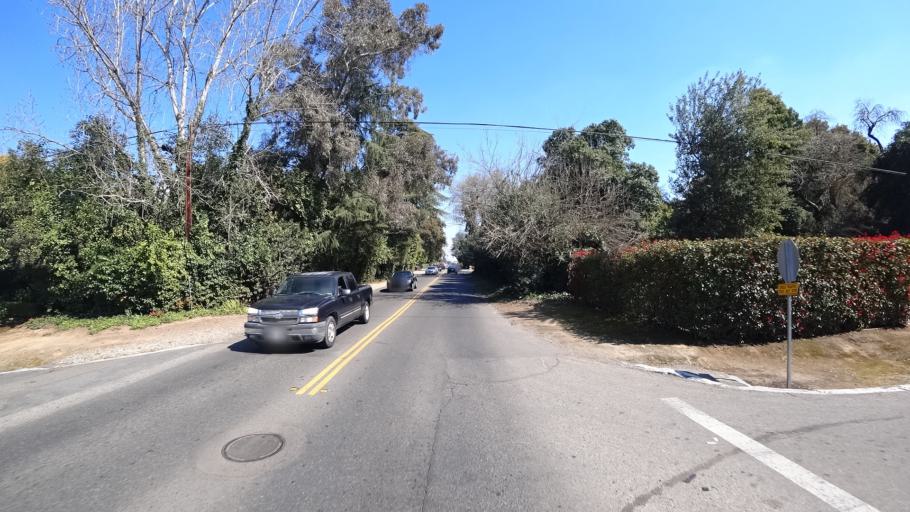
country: US
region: California
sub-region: Fresno County
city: Fresno
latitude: 36.7940
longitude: -119.8025
